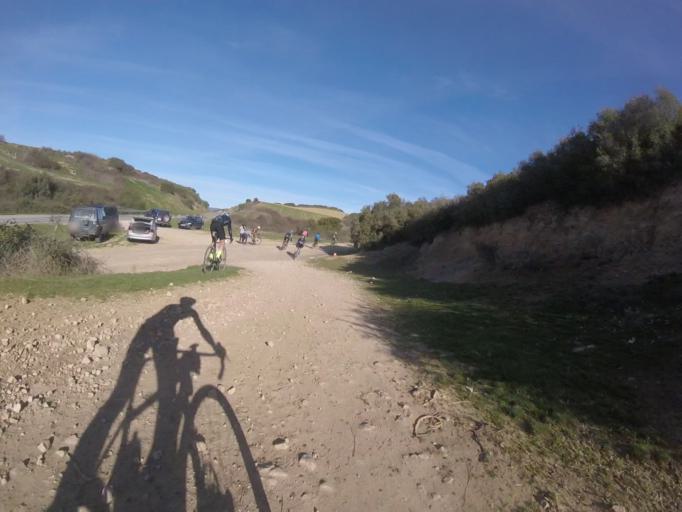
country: ES
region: Navarre
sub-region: Provincia de Navarra
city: Yerri
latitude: 42.7005
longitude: -1.9662
